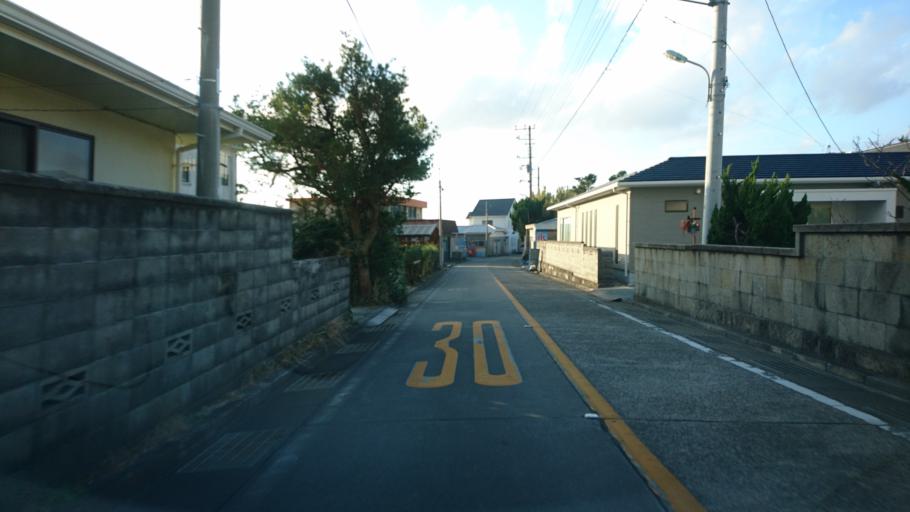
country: JP
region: Shizuoka
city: Shimoda
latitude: 34.3728
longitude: 139.2583
